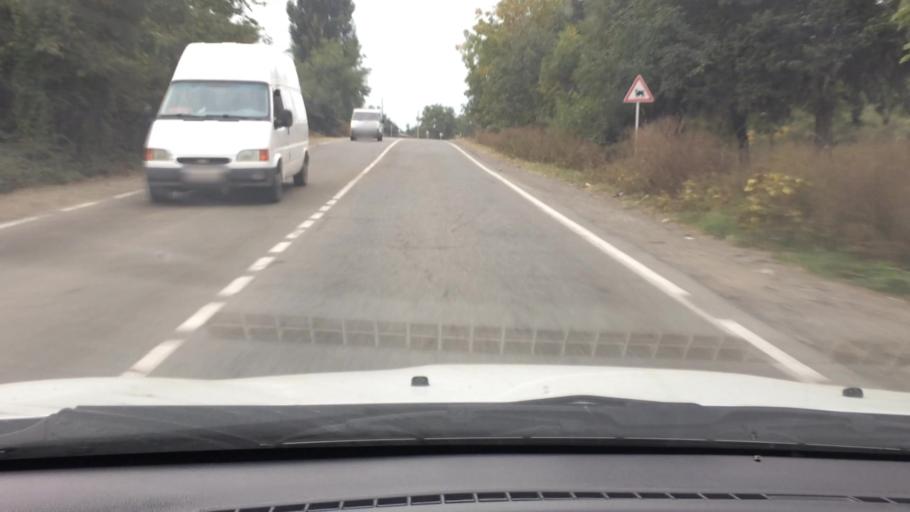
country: AM
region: Tavush
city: Bagratashen
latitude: 41.2974
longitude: 44.7889
